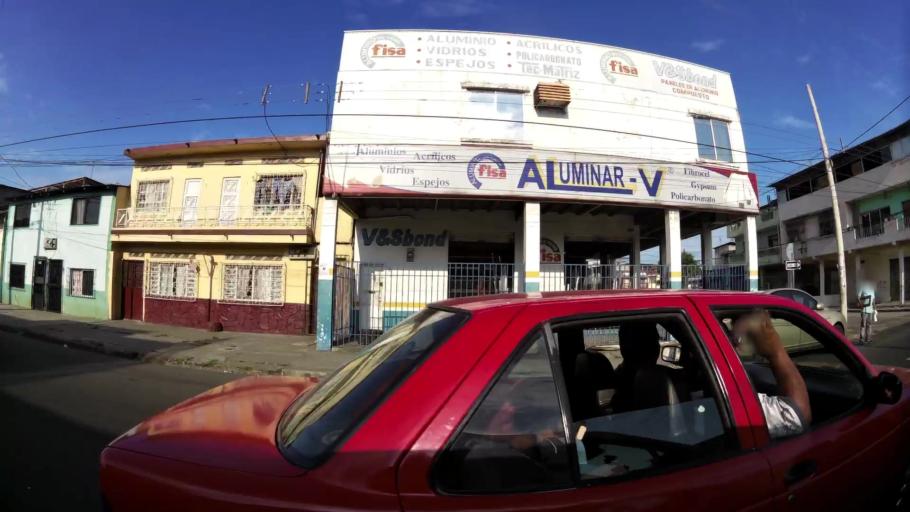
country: EC
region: Guayas
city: Guayaquil
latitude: -2.2132
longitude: -79.9018
